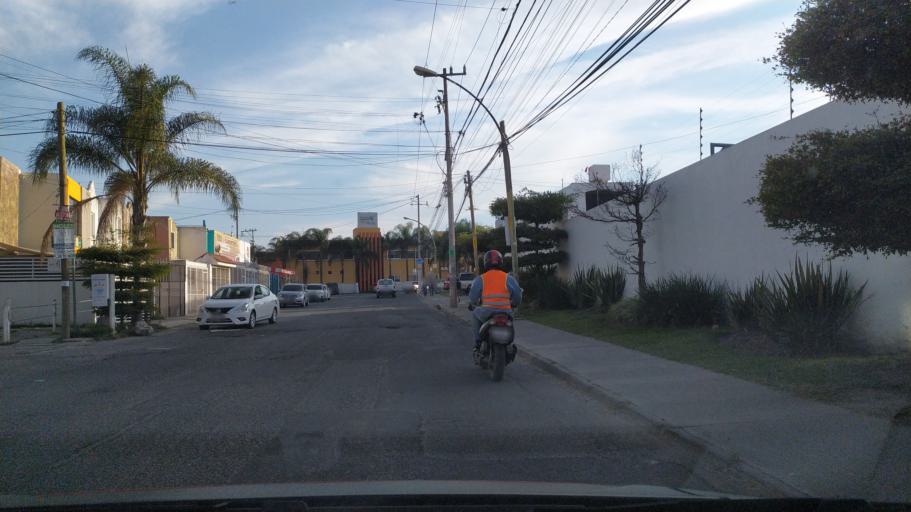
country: MX
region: Jalisco
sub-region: Tlajomulco de Zuniga
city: Palomar
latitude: 20.6260
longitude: -103.4554
